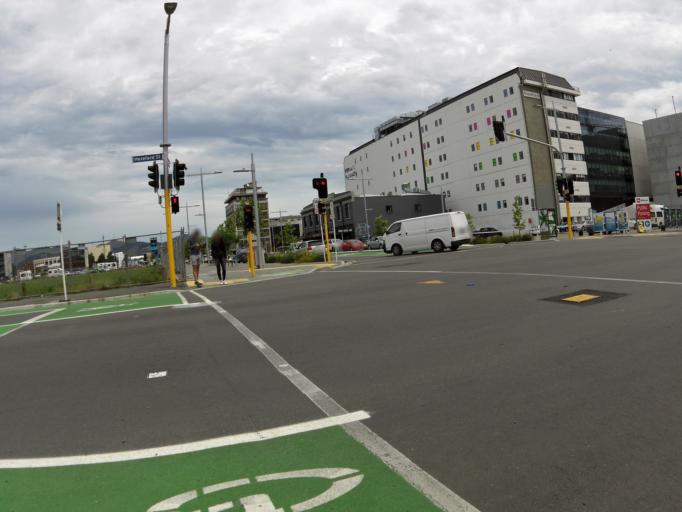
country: NZ
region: Canterbury
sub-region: Christchurch City
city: Christchurch
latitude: -43.5322
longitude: 172.6397
